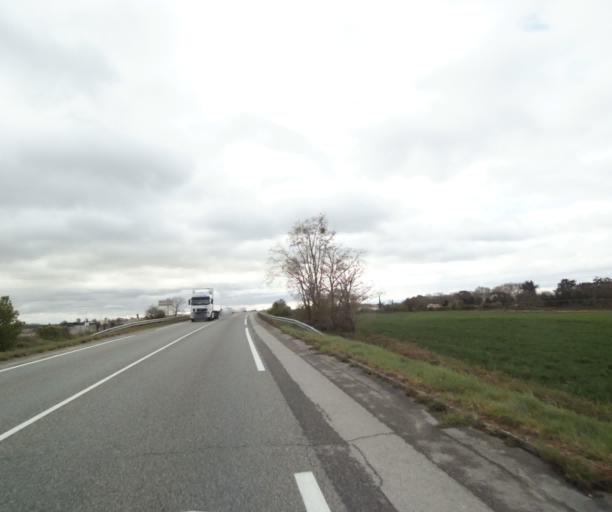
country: FR
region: Midi-Pyrenees
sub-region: Departement de l'Ariege
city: Saverdun
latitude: 43.2335
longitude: 1.6001
